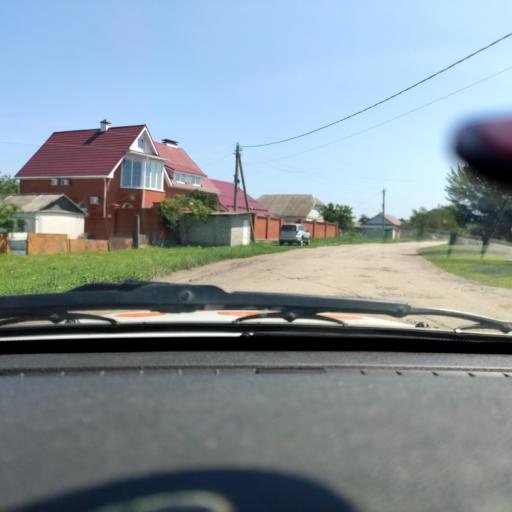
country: RU
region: Voronezj
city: Devitsa
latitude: 51.5964
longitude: 38.9850
